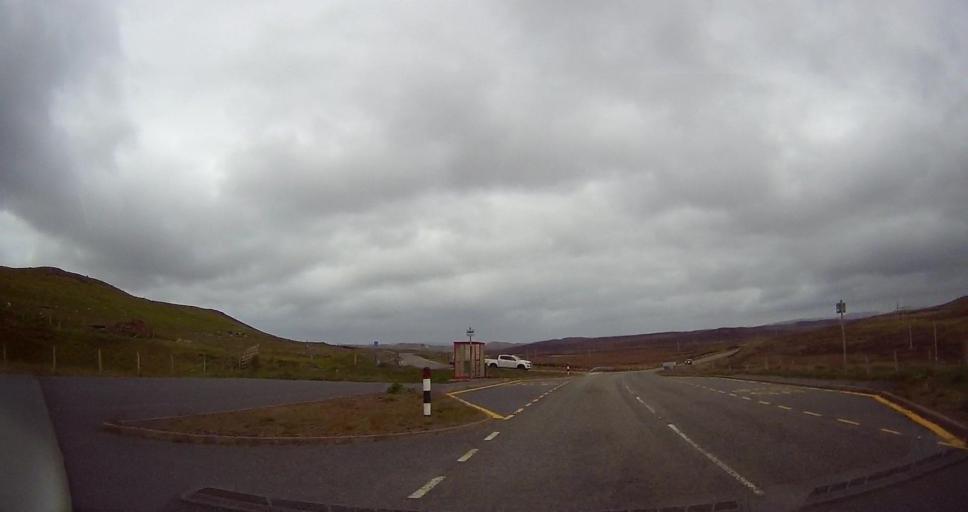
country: GB
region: Scotland
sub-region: Shetland Islands
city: Sandwick
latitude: 60.2562
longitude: -1.4998
